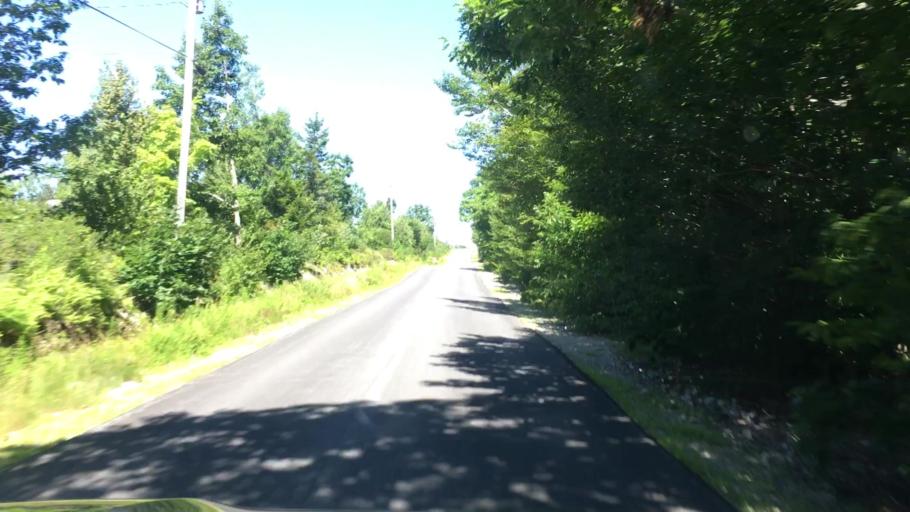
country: US
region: Maine
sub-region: Hancock County
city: Sedgwick
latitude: 44.3212
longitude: -68.6314
